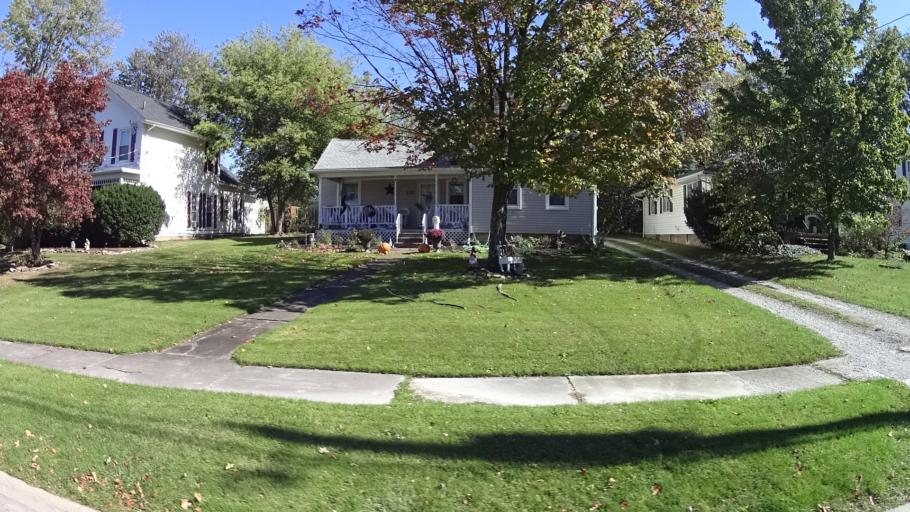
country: US
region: Ohio
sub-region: Lorain County
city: Amherst
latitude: 41.3939
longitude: -82.2208
